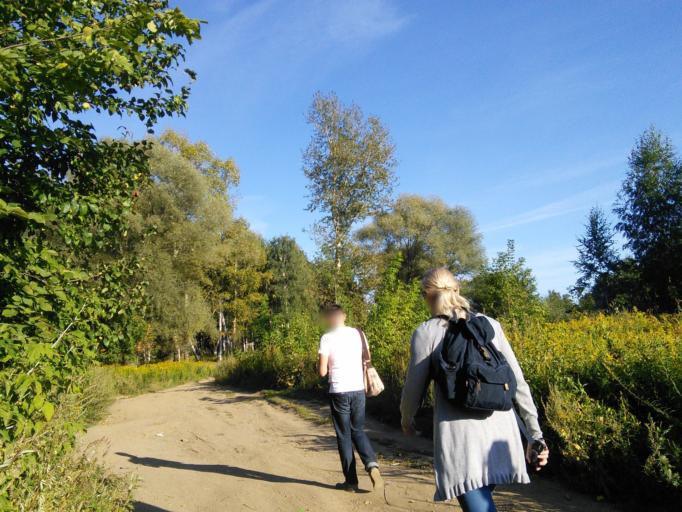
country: RU
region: Moskovskaya
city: Pavlovskiy Posad
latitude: 55.7881
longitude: 38.6808
